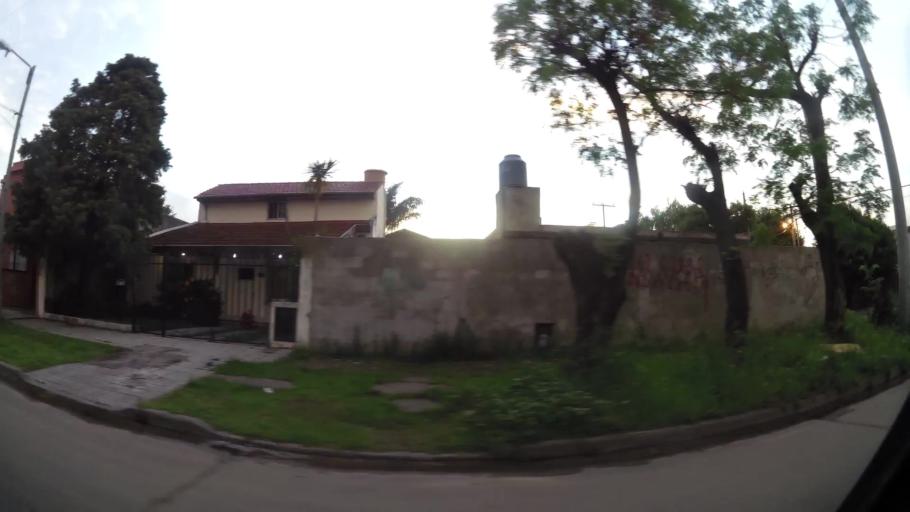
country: AR
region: Buenos Aires
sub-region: Partido de Lomas de Zamora
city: Lomas de Zamora
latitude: -34.7617
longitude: -58.3758
